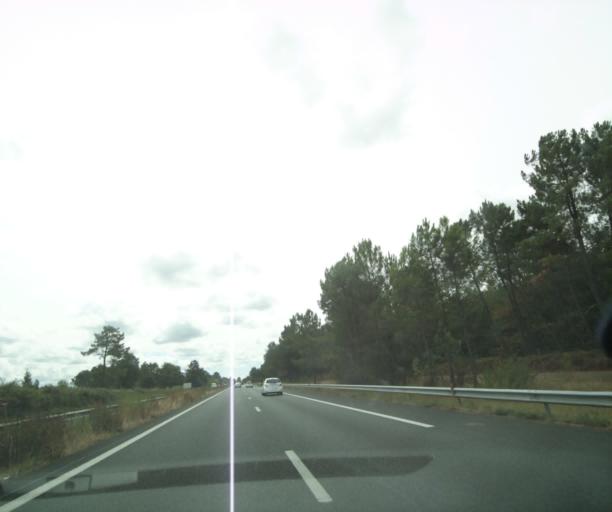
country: FR
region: Aquitaine
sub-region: Departement de la Gironde
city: Reignac
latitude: 45.2383
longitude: -0.5310
